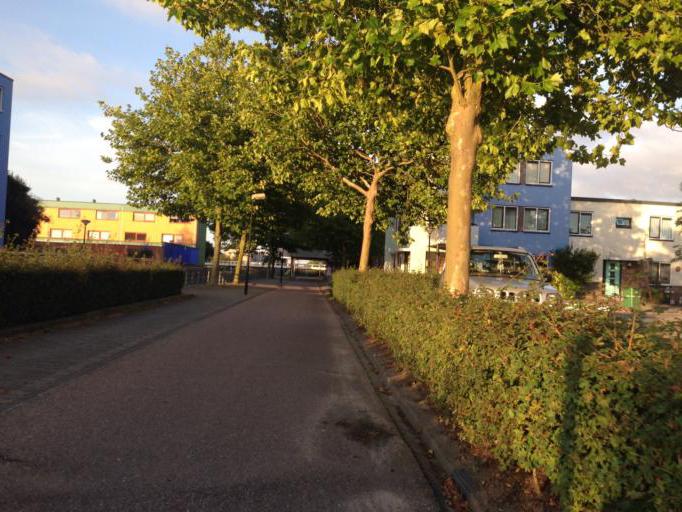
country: NL
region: Flevoland
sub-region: Gemeente Almere
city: Almere Stad
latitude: 52.3955
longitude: 5.2990
